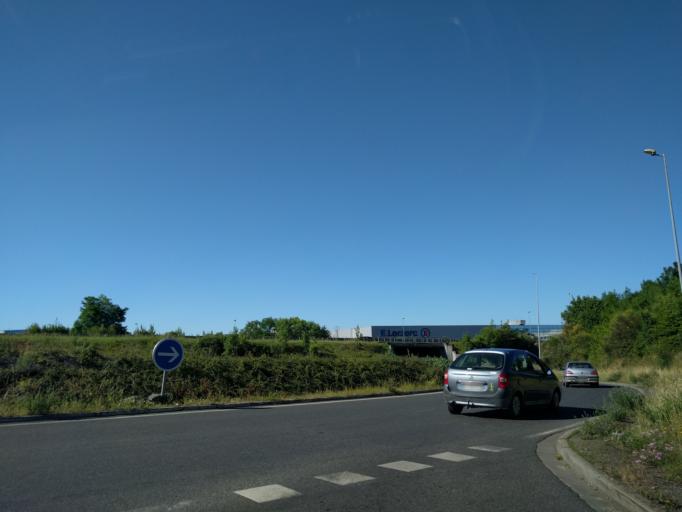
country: FR
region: Poitou-Charentes
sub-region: Departement des Deux-Sevres
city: Chauray
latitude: 46.3400
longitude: -0.4087
